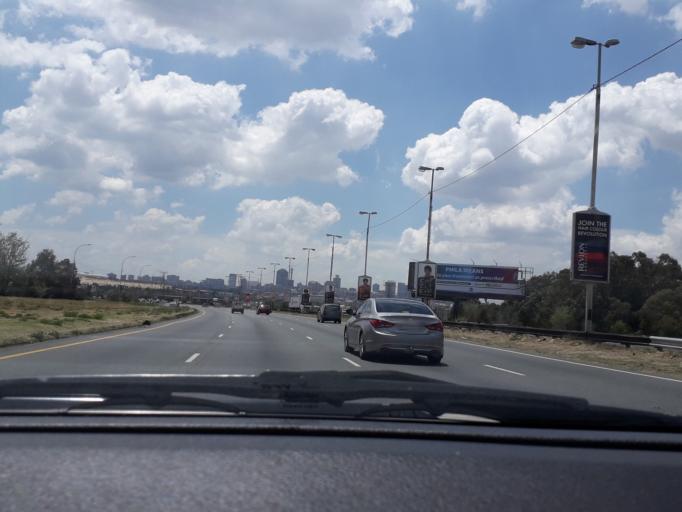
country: ZA
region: Gauteng
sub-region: City of Johannesburg Metropolitan Municipality
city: Johannesburg
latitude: -26.2363
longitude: 28.0176
